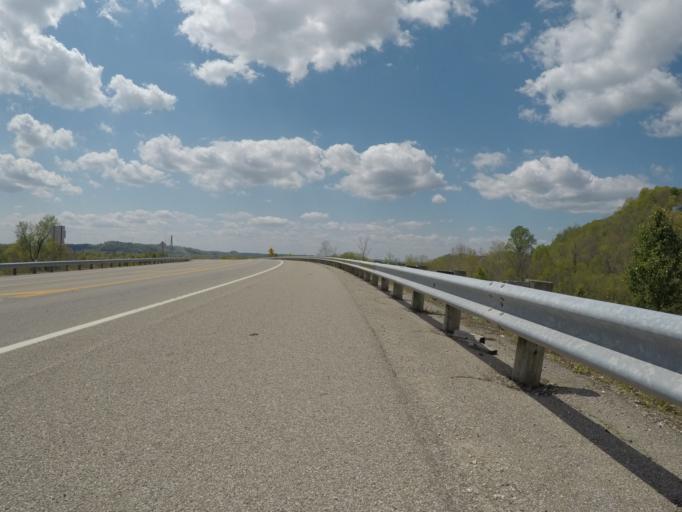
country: US
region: West Virginia
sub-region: Cabell County
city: Pea Ridge
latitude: 38.4481
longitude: -82.3784
